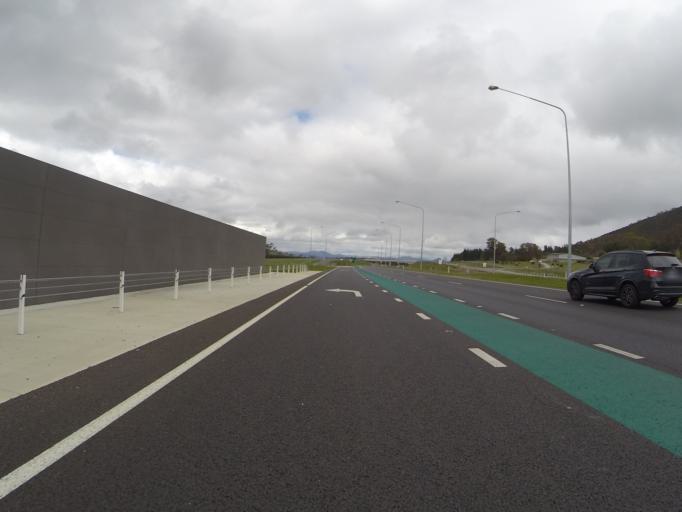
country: AU
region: Australian Capital Territory
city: Canberra
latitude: -35.2287
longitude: 149.1966
